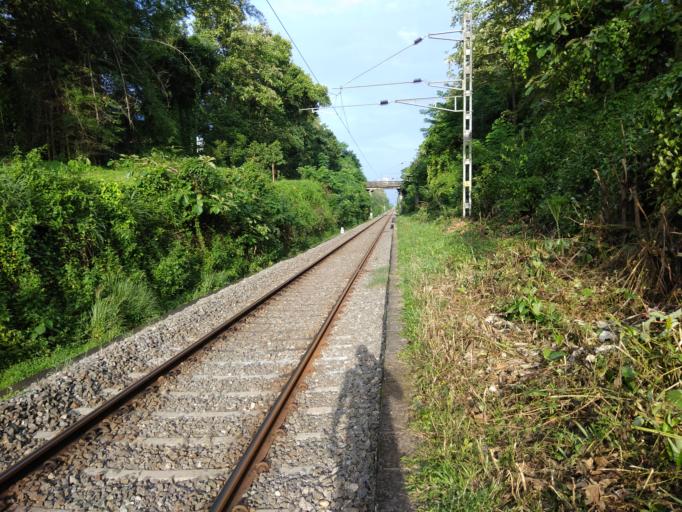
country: IN
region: Kerala
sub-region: Thrissur District
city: Avanoor
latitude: 10.5620
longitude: 76.1727
